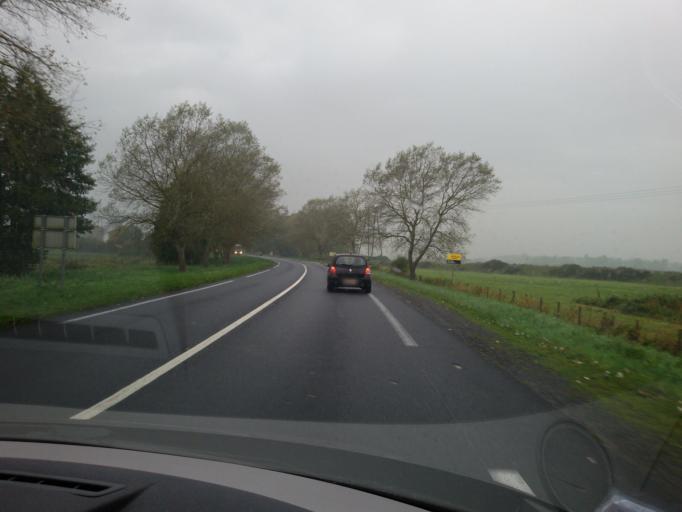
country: FR
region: Lower Normandy
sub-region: Departement du Calvados
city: Ablon
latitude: 49.4120
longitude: 0.2970
